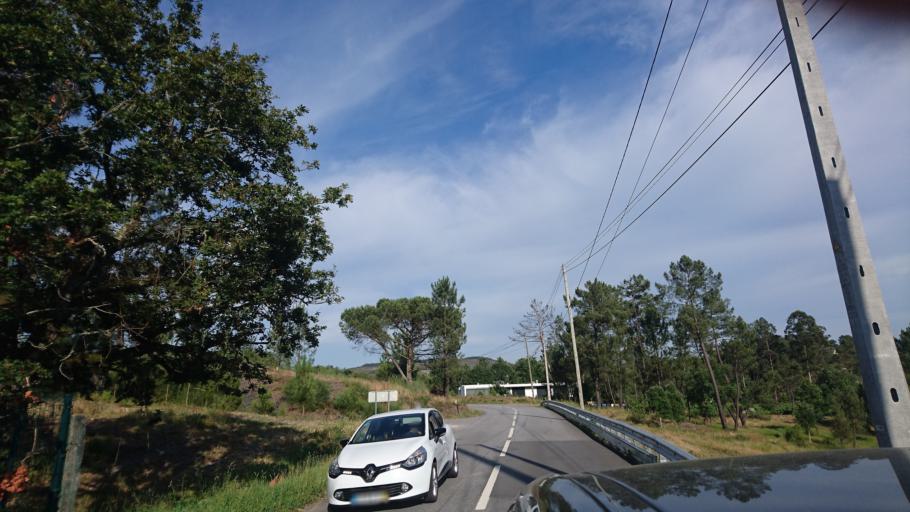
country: PT
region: Porto
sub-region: Paredes
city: Recarei
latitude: 41.1337
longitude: -8.4238
